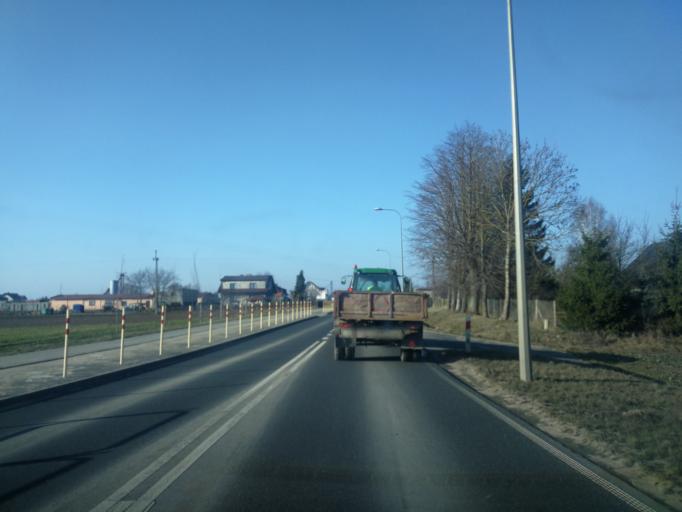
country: PL
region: Warmian-Masurian Voivodeship
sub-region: Powiat ilawski
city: Lubawa
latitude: 53.4690
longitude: 19.7704
